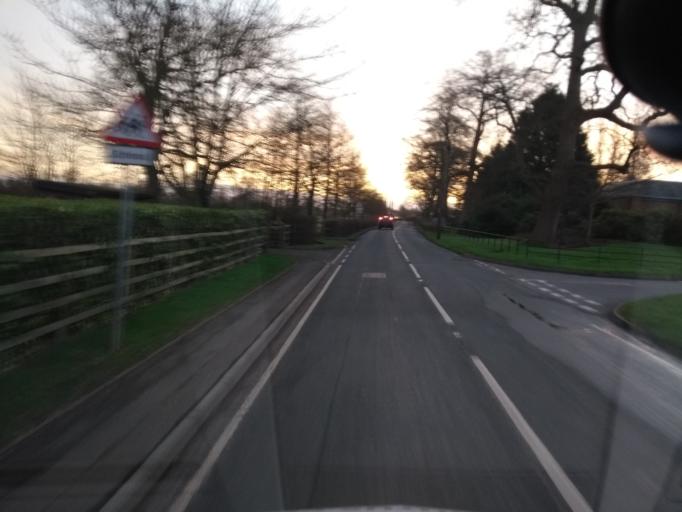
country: GB
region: England
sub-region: Somerset
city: Wedmore
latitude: 51.2269
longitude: -2.8862
